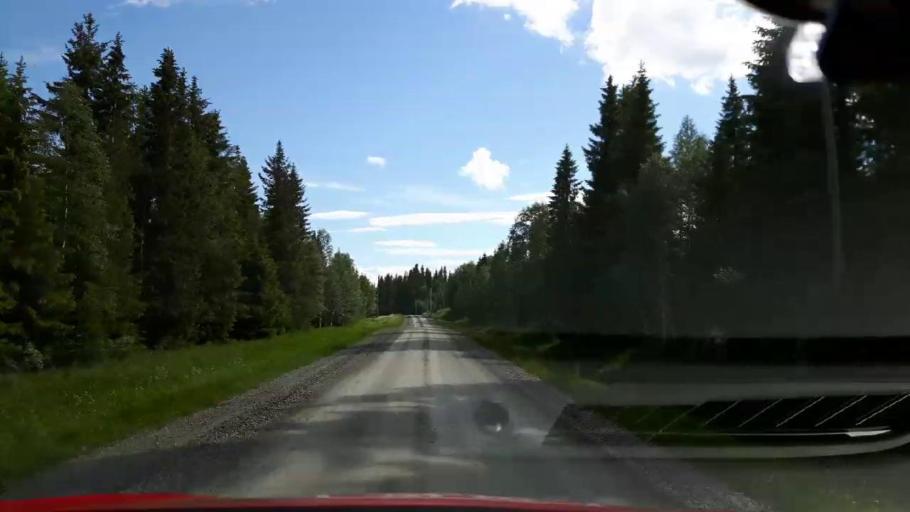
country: SE
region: Jaemtland
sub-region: Krokoms Kommun
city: Valla
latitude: 63.8028
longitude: 14.0485
